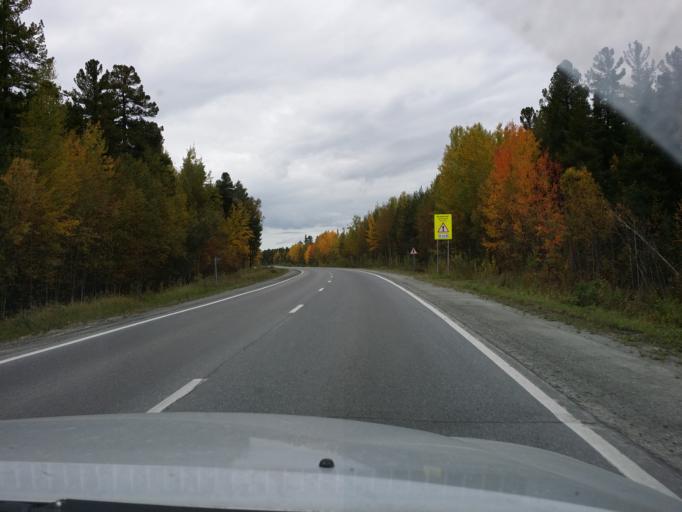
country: RU
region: Khanty-Mansiyskiy Avtonomnyy Okrug
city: Langepas
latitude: 61.2152
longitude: 75.3597
